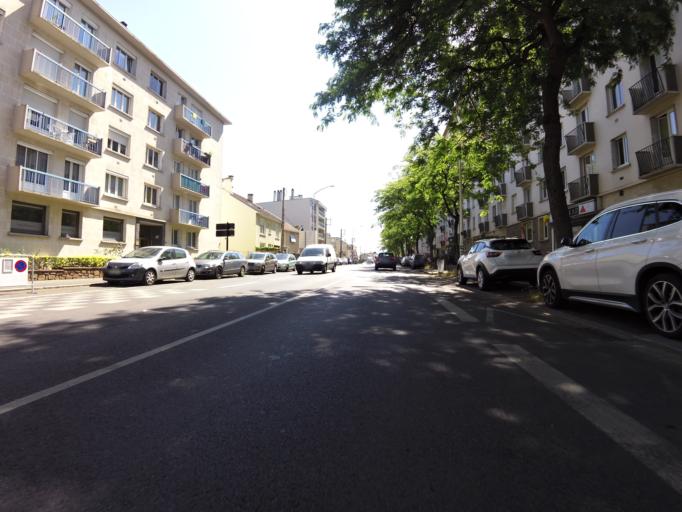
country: FR
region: Pays de la Loire
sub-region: Departement de la Loire-Atlantique
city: Nantes
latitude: 47.2373
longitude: -1.5864
